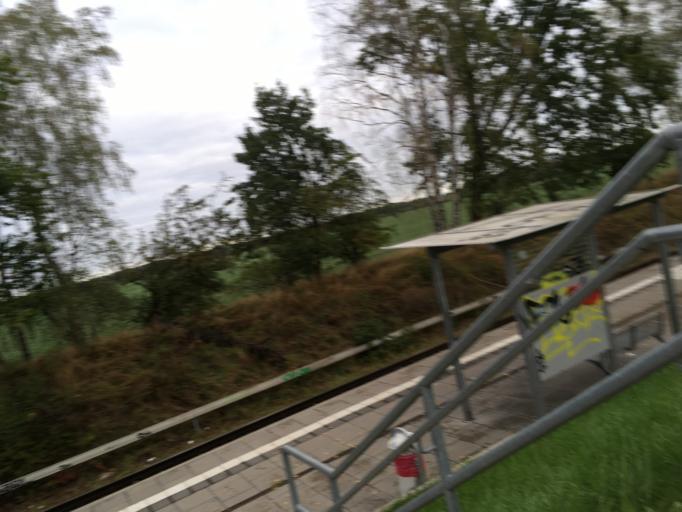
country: DE
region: Brandenburg
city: Ahrensfelde
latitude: 52.5968
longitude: 13.5922
